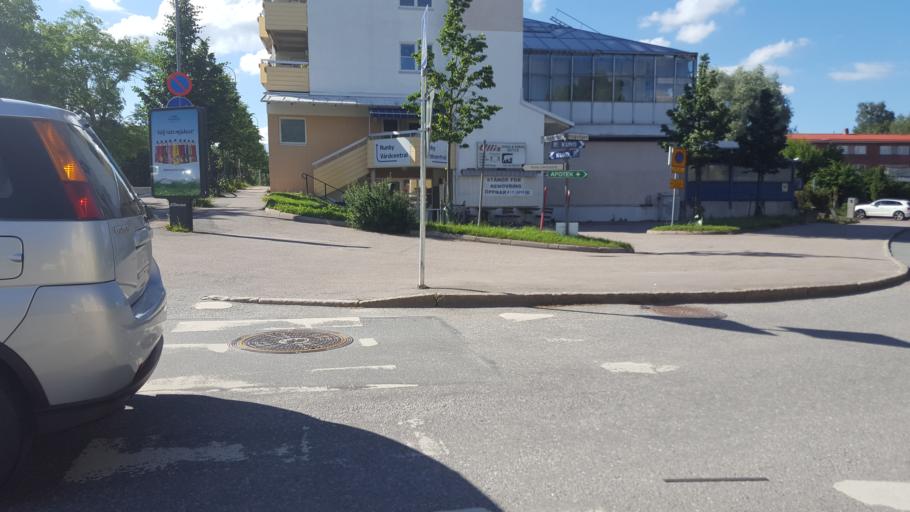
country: SE
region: Stockholm
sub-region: Upplands Vasby Kommun
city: Upplands Vaesby
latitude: 59.5195
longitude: 17.8938
